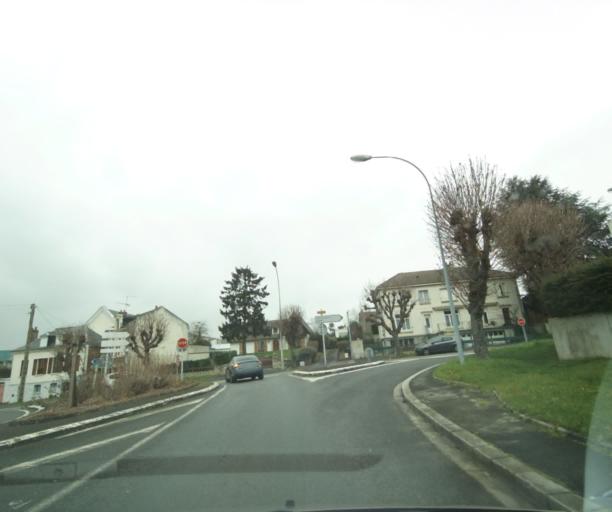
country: FR
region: Picardie
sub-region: Departement de l'Oise
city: Noyon
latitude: 49.5845
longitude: 2.9995
